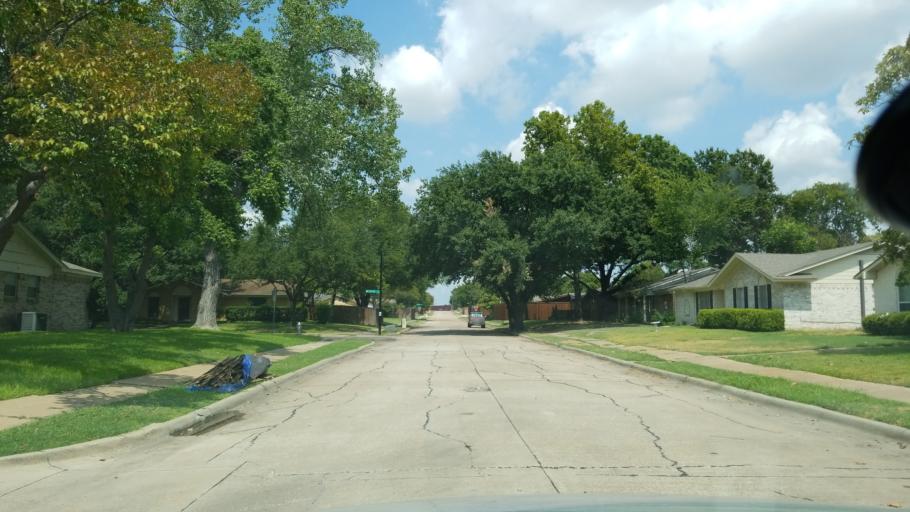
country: US
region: Texas
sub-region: Dallas County
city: Garland
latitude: 32.9253
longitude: -96.6537
